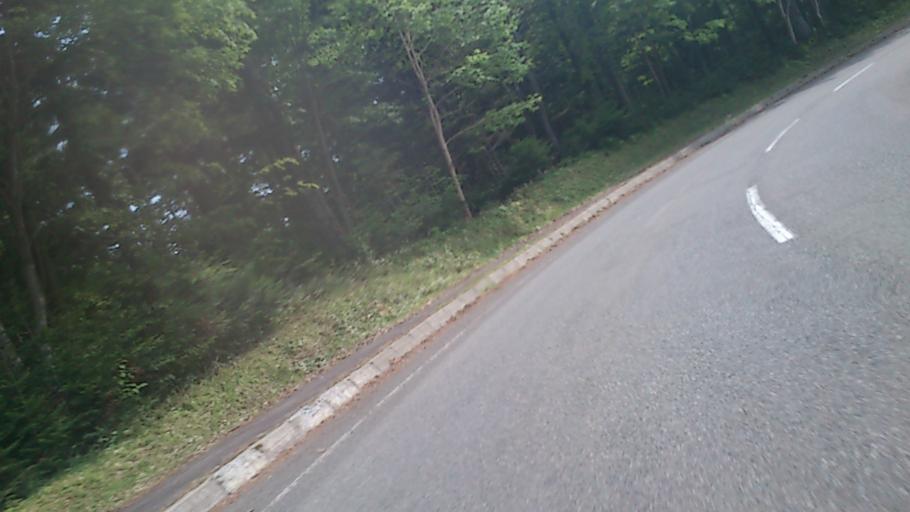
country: JP
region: Hokkaido
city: Kitami
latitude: 43.3913
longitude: 143.9704
